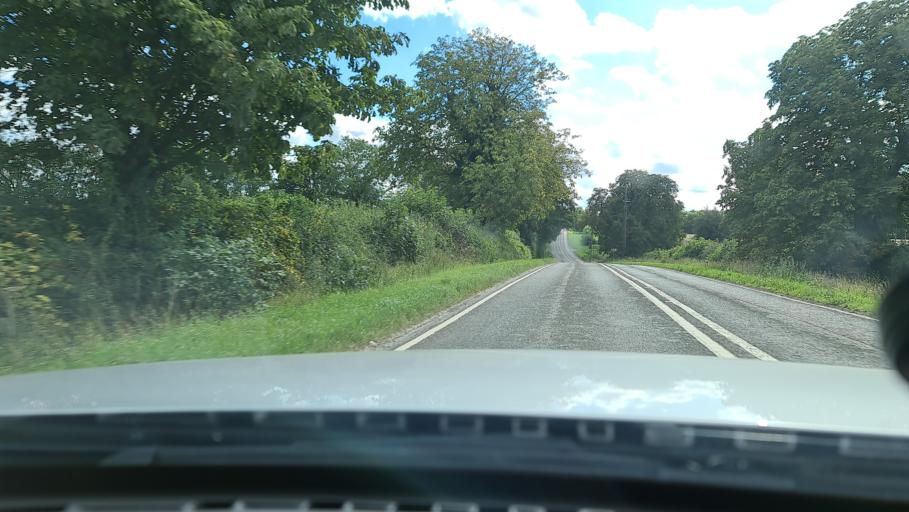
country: GB
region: England
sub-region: Oxfordshire
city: Somerton
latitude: 51.9152
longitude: -1.2241
